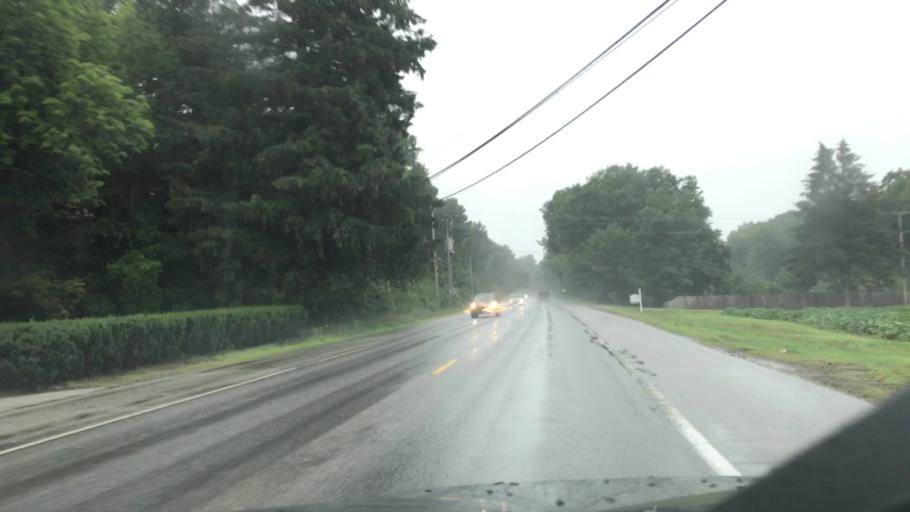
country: US
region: Maine
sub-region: York County
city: North Berwick
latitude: 43.3069
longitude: -70.6752
